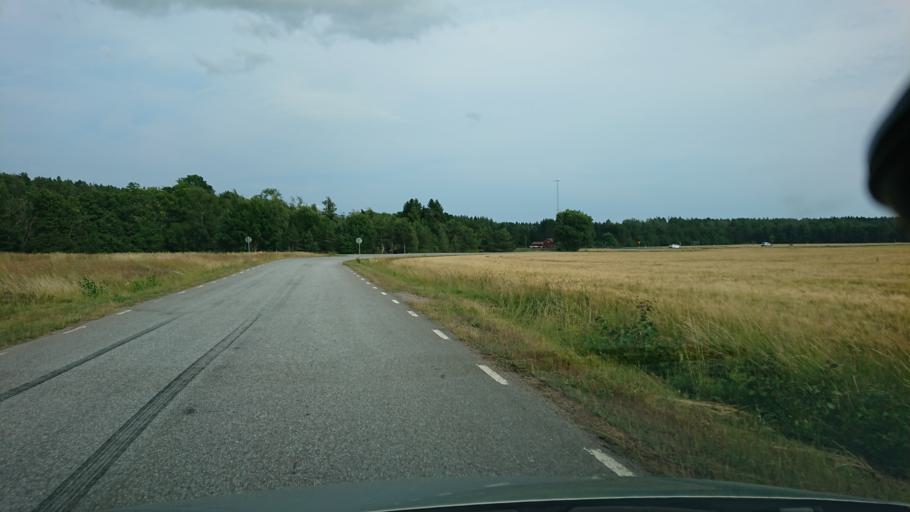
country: SE
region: Uppsala
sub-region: Osthammars Kommun
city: Bjorklinge
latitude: 59.9749
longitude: 17.5744
